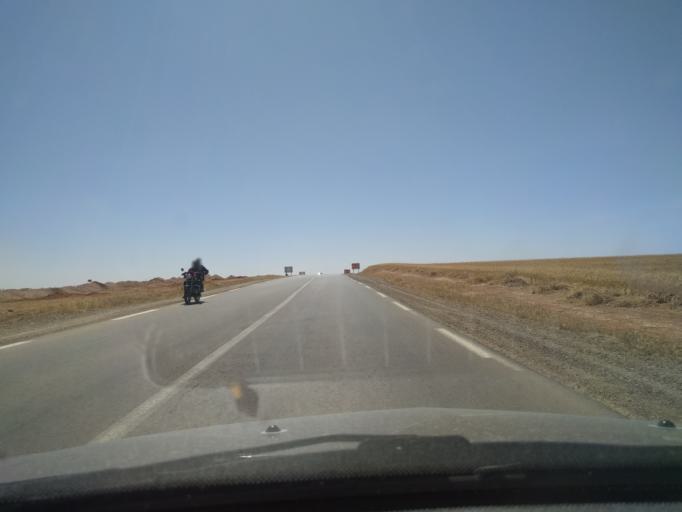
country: DZ
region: Tiaret
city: Frenda
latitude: 34.8944
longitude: 1.1693
